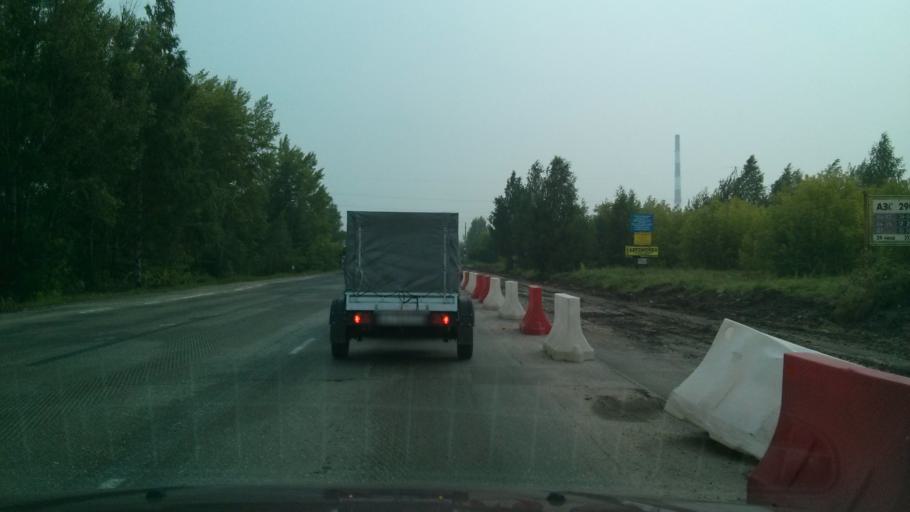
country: RU
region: Nizjnij Novgorod
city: Kstovo
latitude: 56.1184
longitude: 44.1539
